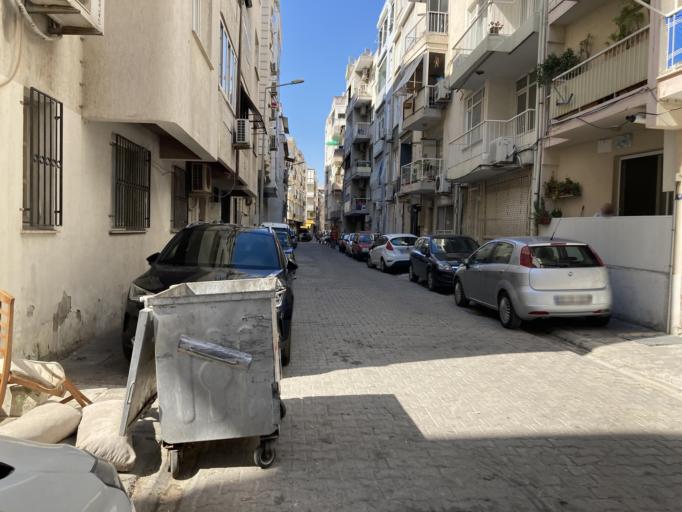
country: TR
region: Izmir
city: Karsiyaka
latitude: 38.4570
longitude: 27.1214
